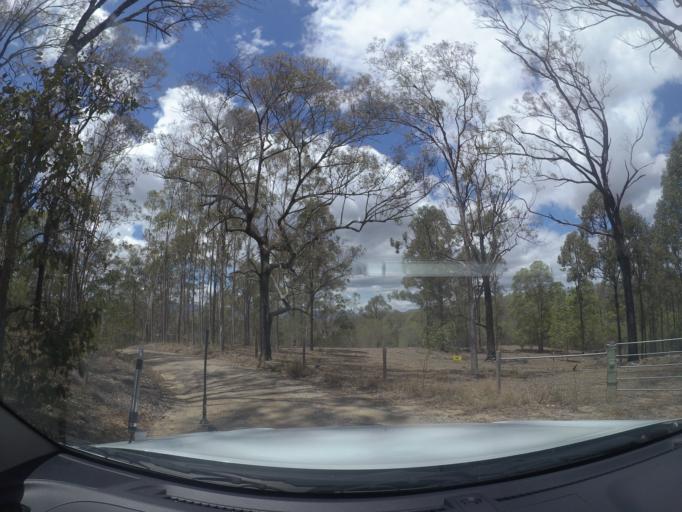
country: AU
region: Queensland
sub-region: Logan
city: Cedar Vale
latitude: -27.9167
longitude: 153.0478
